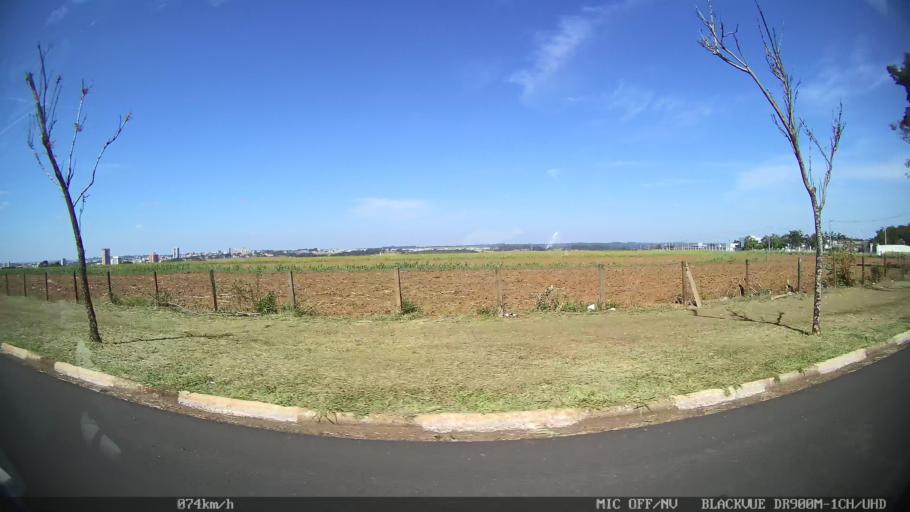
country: BR
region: Sao Paulo
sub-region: Franca
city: Franca
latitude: -20.5506
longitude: -47.4303
